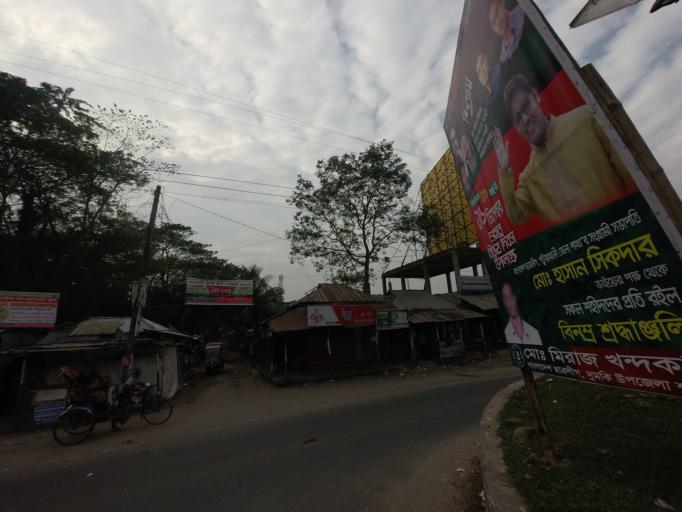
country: BD
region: Barisal
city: Nalchiti
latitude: 22.4536
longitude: 90.3408
